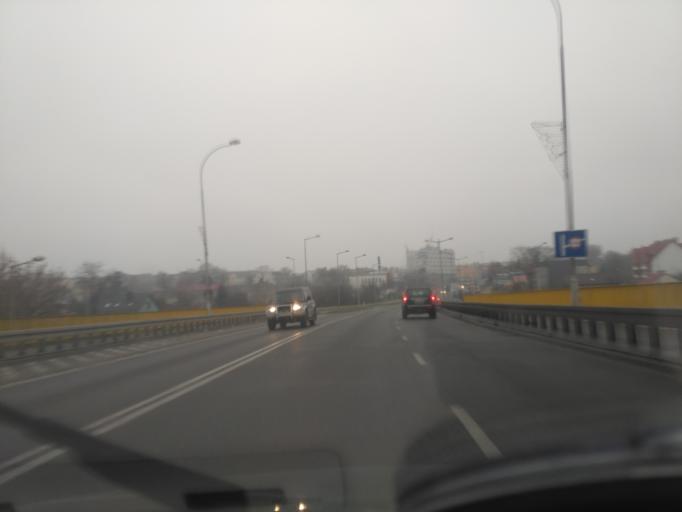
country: PL
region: Lublin Voivodeship
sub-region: Chelm
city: Chelm
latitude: 51.1390
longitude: 23.4698
